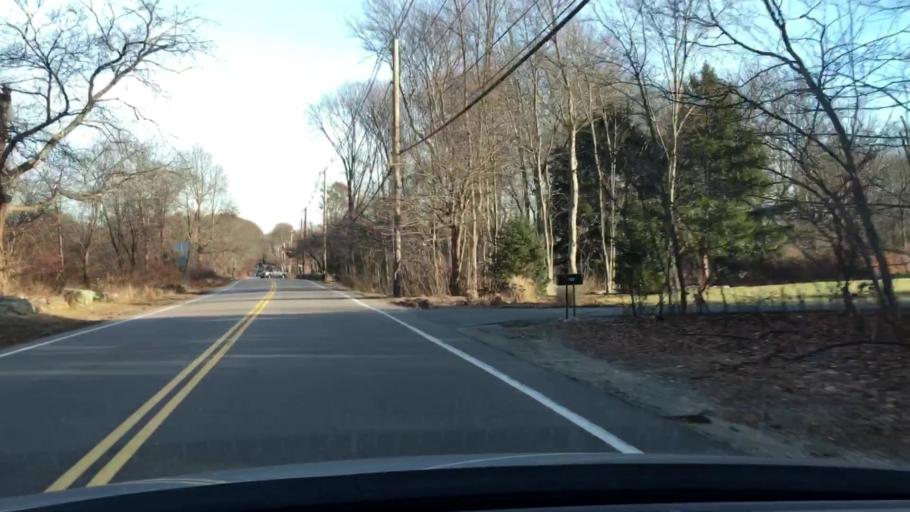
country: US
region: Massachusetts
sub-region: Norfolk County
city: Westwood
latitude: 42.2219
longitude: -71.2121
